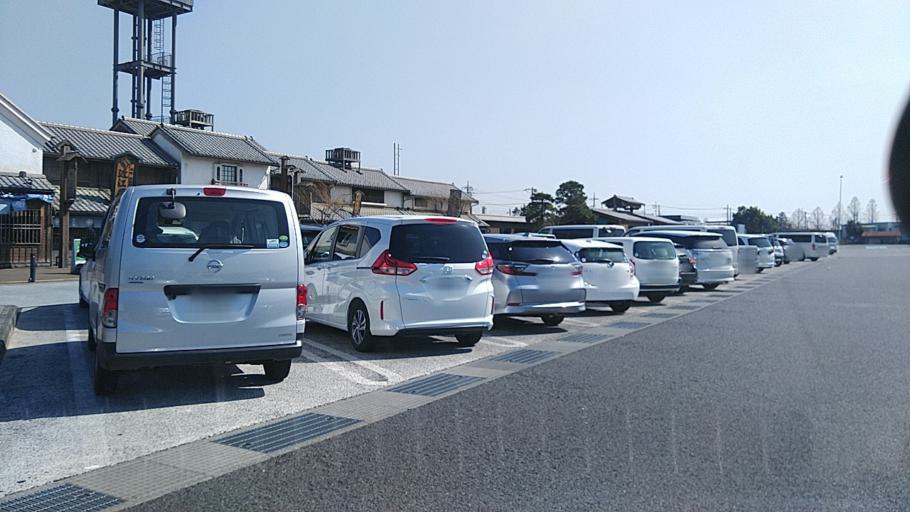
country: JP
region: Saitama
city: Hanyu
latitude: 36.1818
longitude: 139.5877
